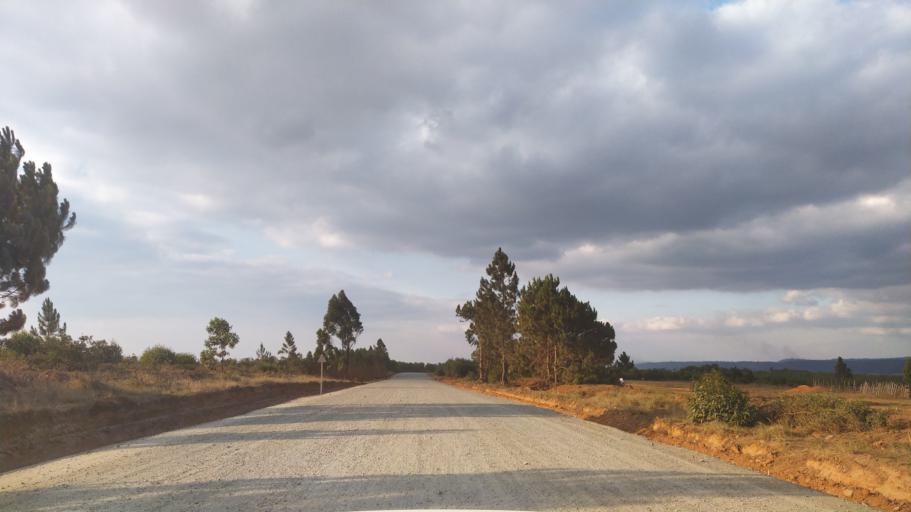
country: MG
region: Analamanga
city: Anjozorobe
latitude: -18.5219
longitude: 48.2624
